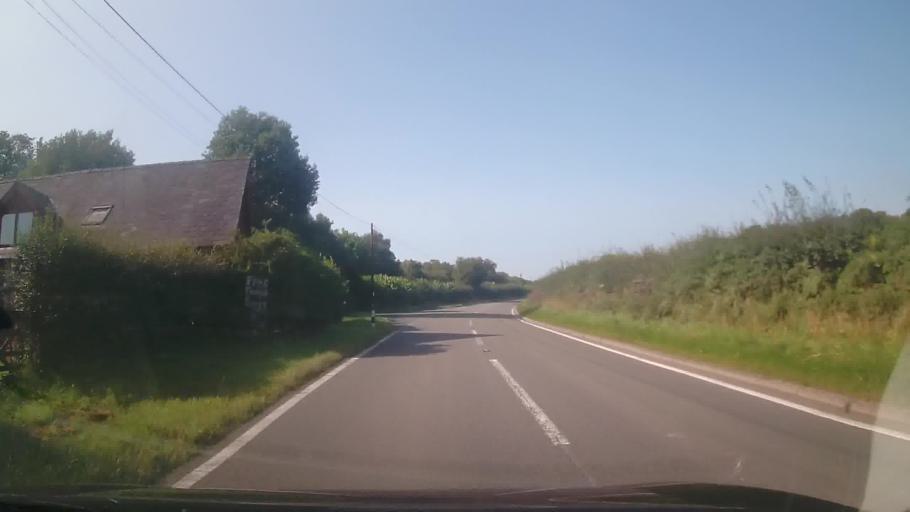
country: GB
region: Wales
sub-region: Sir Powys
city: Builth Wells
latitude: 52.1442
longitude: -3.4792
